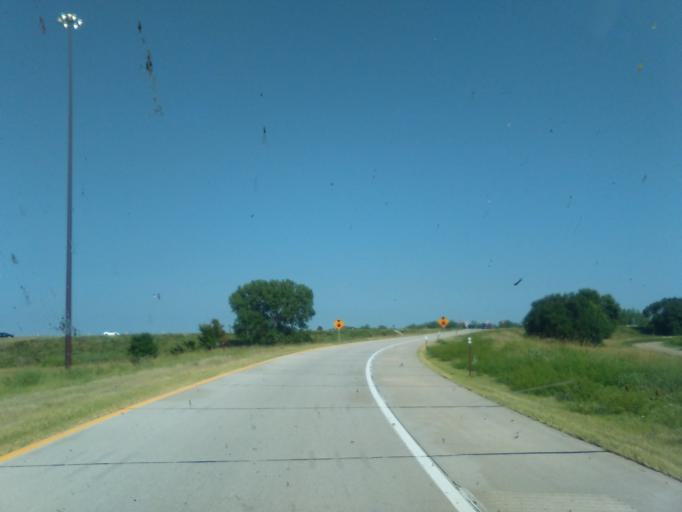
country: US
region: Nebraska
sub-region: Hall County
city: Grand Island
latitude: 40.8192
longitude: -98.3809
